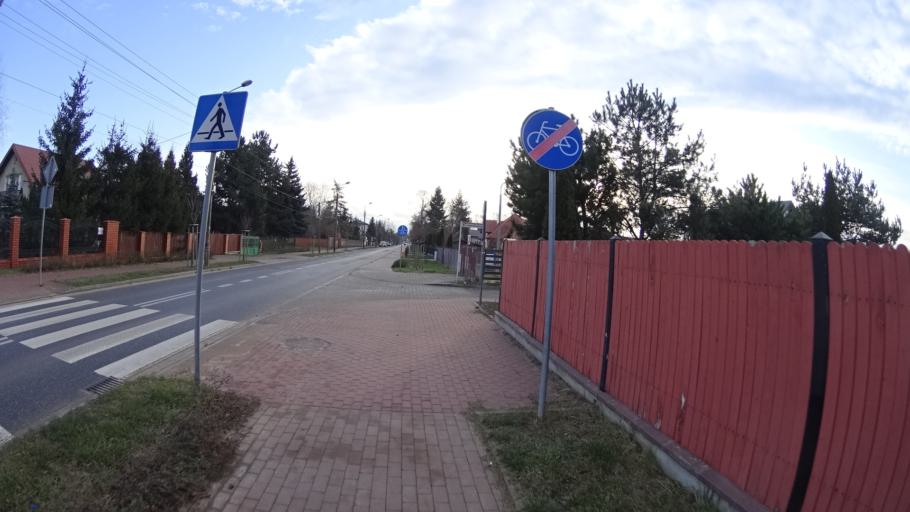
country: PL
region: Masovian Voivodeship
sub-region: Powiat warszawski zachodni
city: Ozarow Mazowiecki
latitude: 52.2204
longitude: 20.8006
